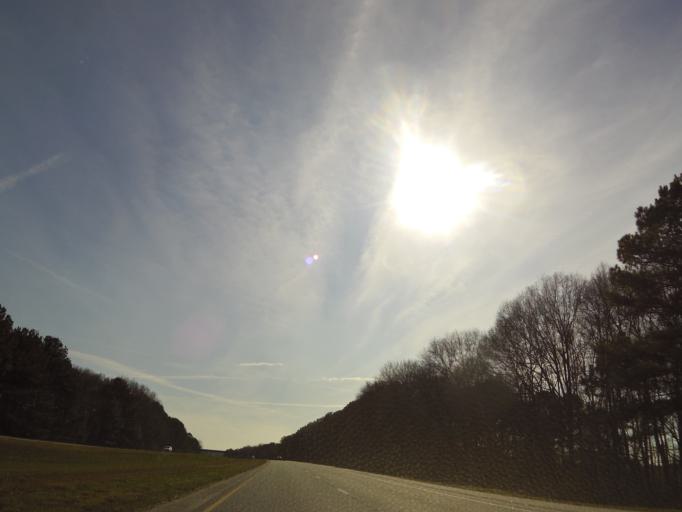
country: US
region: Georgia
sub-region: Harris County
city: Pine Mountain
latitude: 32.8820
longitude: -84.9611
